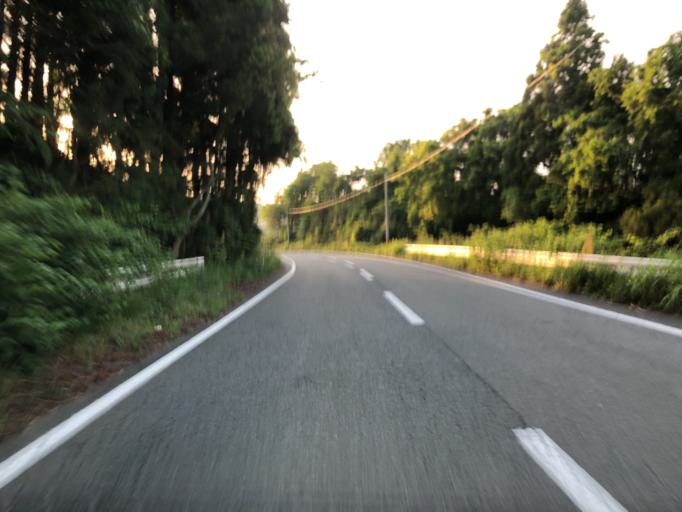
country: JP
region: Fukushima
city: Iwaki
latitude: 37.2408
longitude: 140.9745
